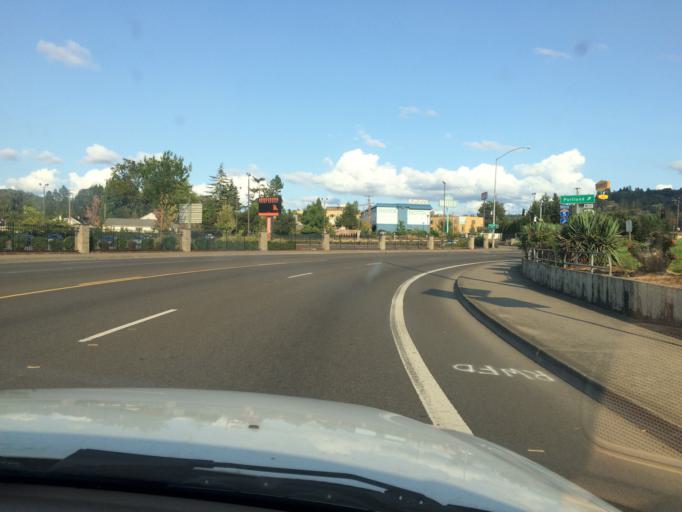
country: US
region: Oregon
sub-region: Douglas County
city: Roseburg
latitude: 43.2138
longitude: -123.3548
